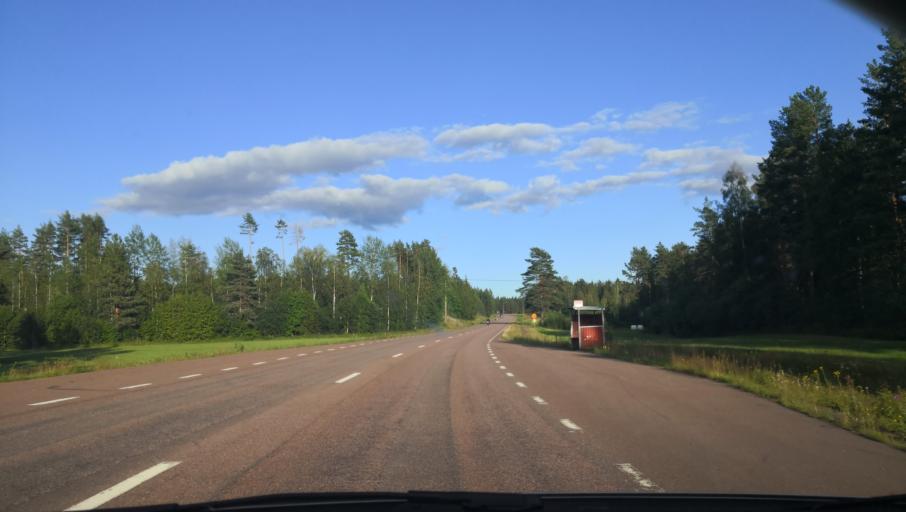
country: SE
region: Dalarna
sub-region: Alvdalens Kommun
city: AElvdalen
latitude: 61.2703
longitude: 13.9985
